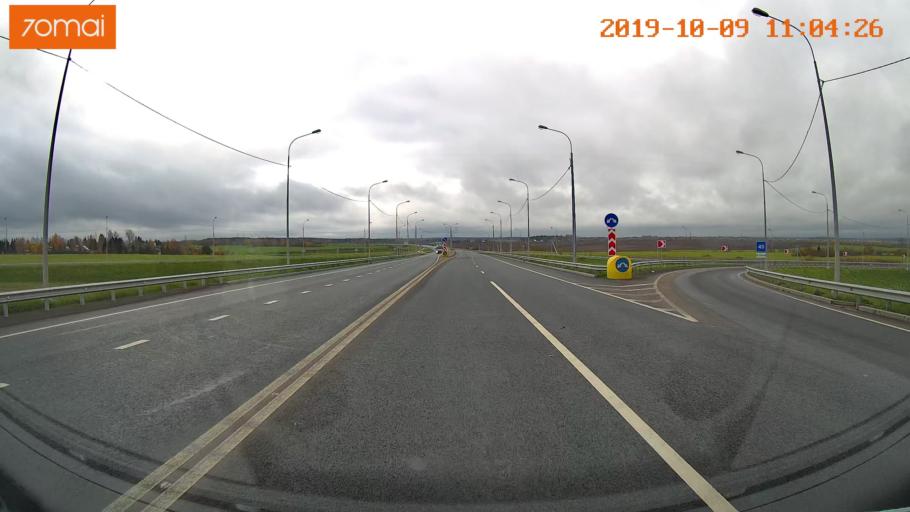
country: RU
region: Vologda
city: Vologda
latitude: 59.2121
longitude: 39.7675
